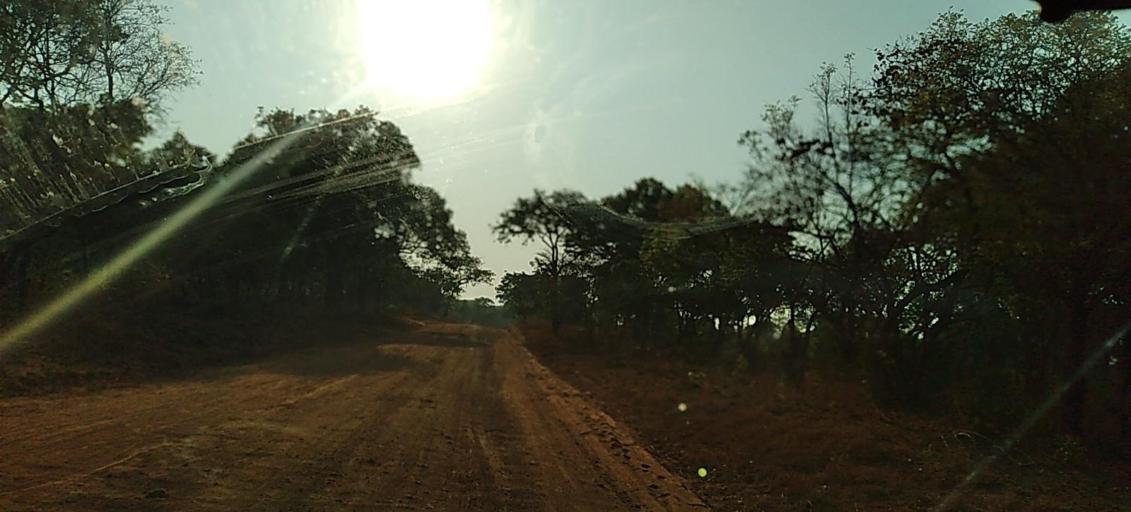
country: ZM
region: North-Western
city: Kasempa
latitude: -13.4719
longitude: 25.8682
